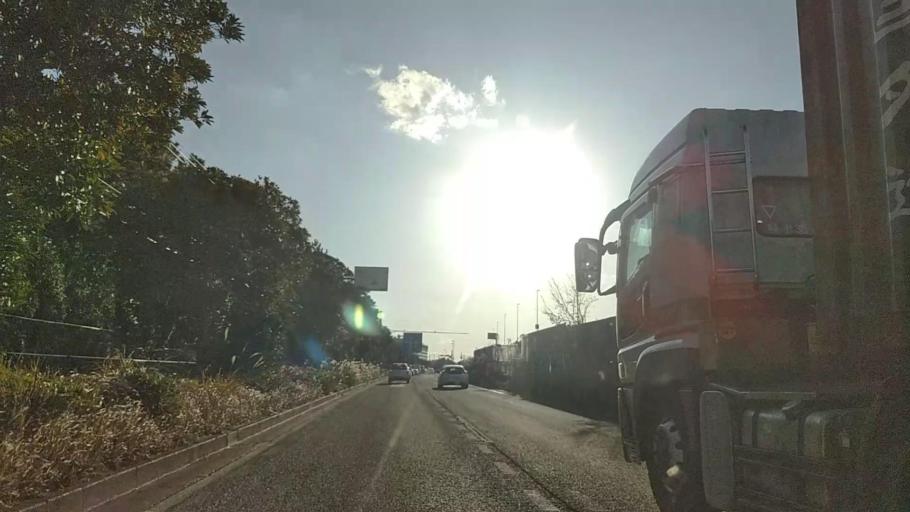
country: JP
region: Tokyo
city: Urayasu
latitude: 35.6625
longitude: 139.9180
